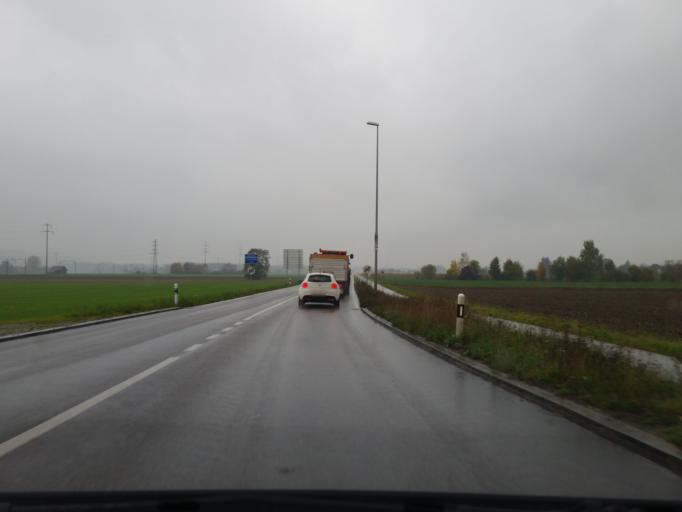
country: CH
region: Thurgau
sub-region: Weinfelden District
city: Weinfelden
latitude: 47.5721
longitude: 9.0959
